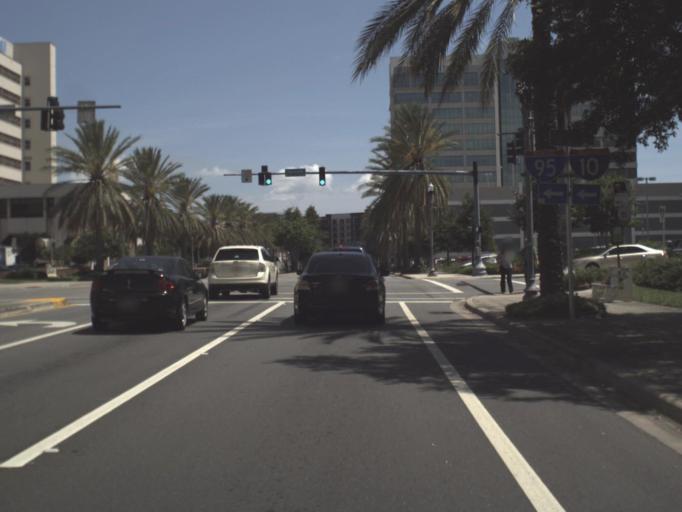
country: US
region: Florida
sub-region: Duval County
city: Jacksonville
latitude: 30.3183
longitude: -81.6756
